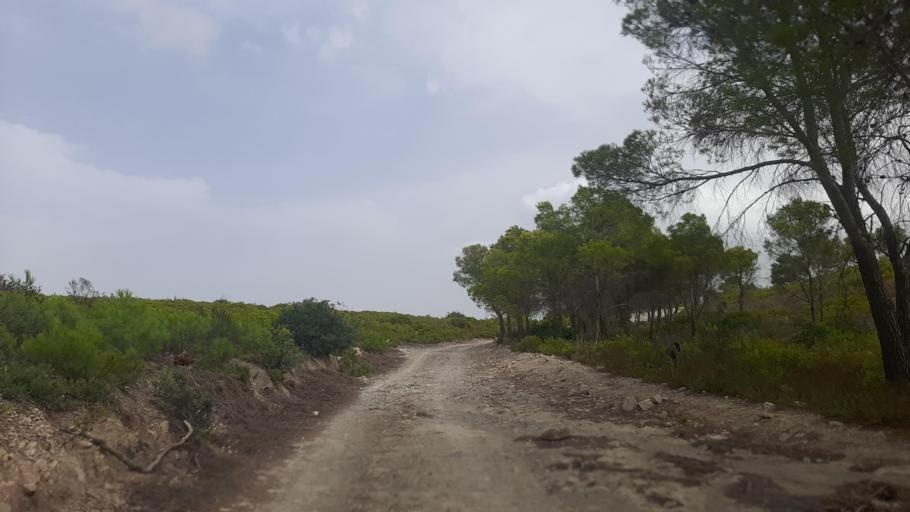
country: TN
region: Zaghwan
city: El Fahs
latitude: 36.1961
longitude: 9.8517
